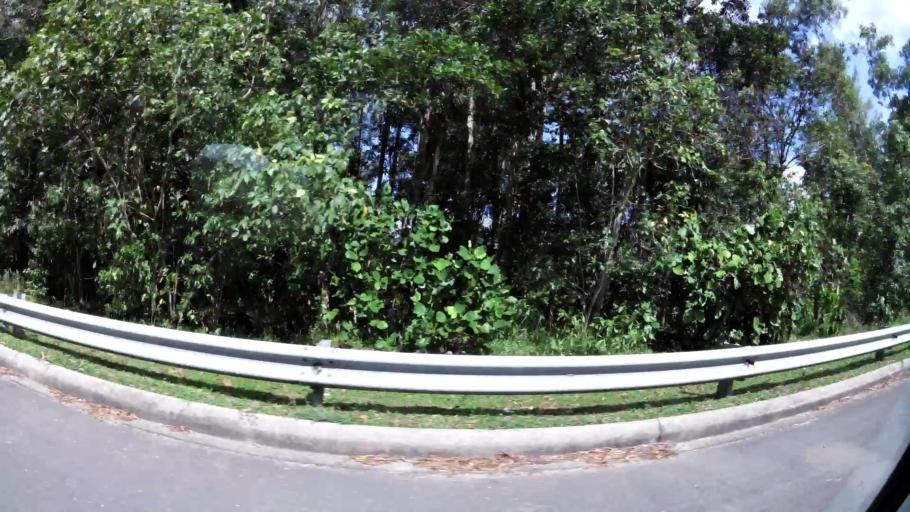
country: BN
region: Brunei and Muara
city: Bandar Seri Begawan
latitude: 4.9590
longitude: 114.9507
